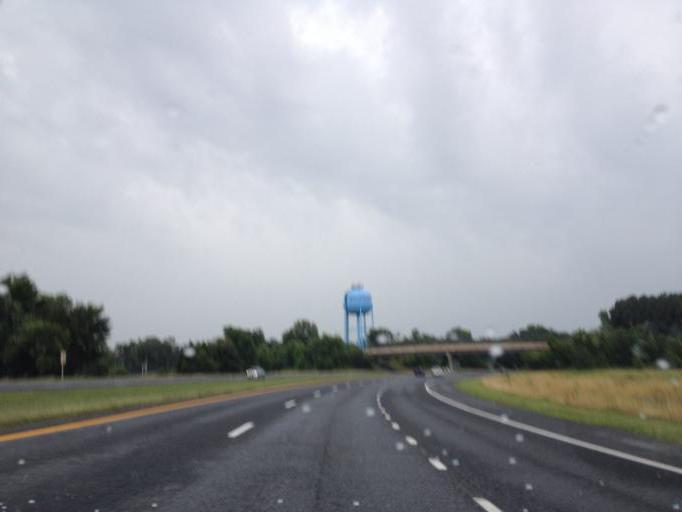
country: US
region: Maryland
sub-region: Caroline County
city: Denton
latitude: 38.8934
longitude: -75.8151
